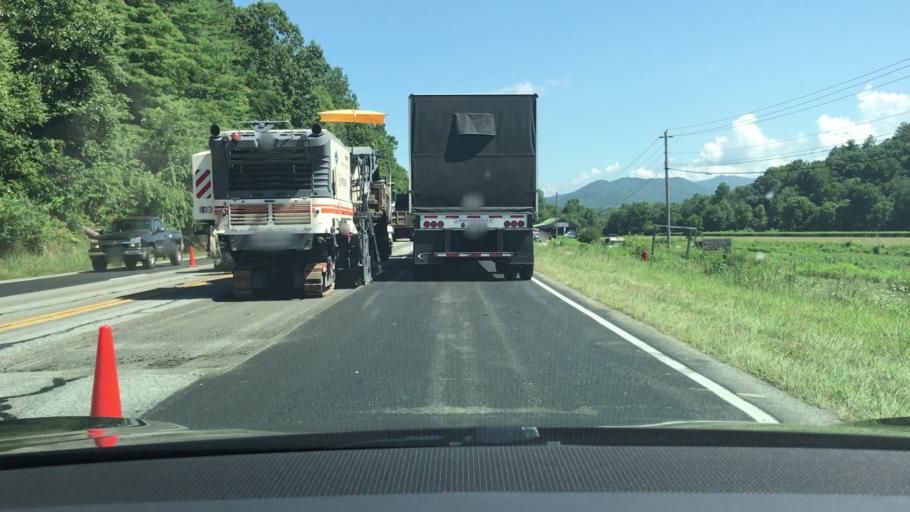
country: US
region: Georgia
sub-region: Rabun County
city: Mountain City
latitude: 34.9460
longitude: -83.3874
